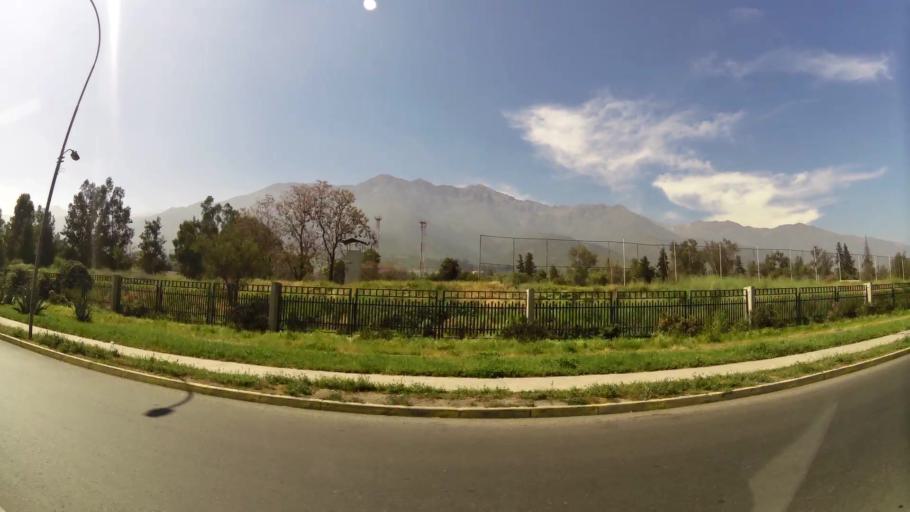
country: CL
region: Santiago Metropolitan
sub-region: Provincia de Santiago
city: Villa Presidente Frei, Nunoa, Santiago, Chile
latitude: -33.4612
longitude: -70.5303
